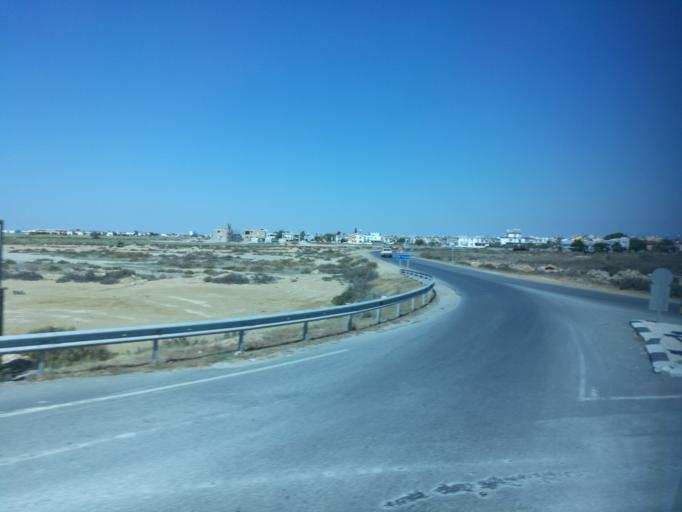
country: CY
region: Ammochostos
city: Famagusta
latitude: 35.1554
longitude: 33.9005
